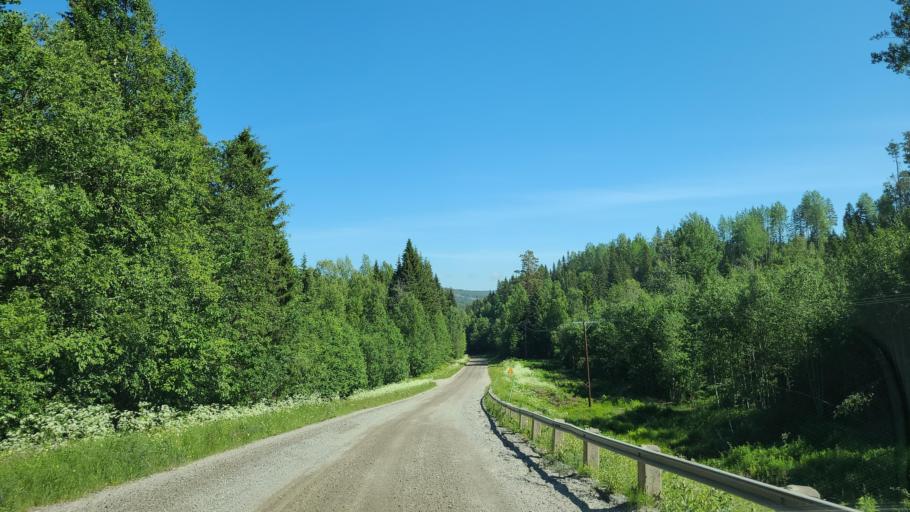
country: SE
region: Vaesterbotten
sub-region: Nordmalings Kommun
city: Nordmaling
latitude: 63.6471
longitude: 19.2303
